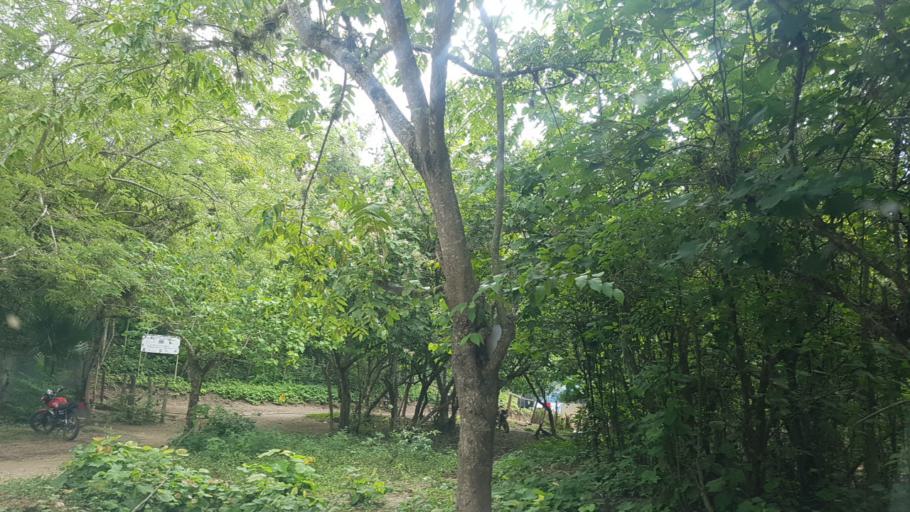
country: NI
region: Nueva Segovia
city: Ciudad Antigua
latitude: 13.6001
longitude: -86.3605
